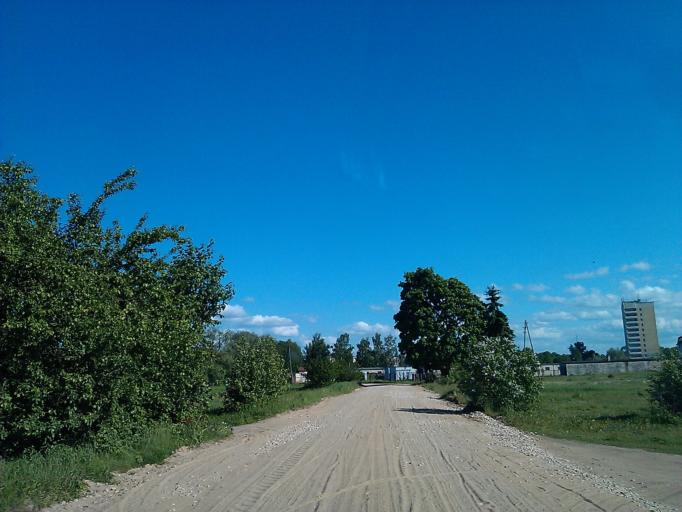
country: LV
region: Adazi
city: Adazi
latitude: 57.0835
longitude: 24.3232
